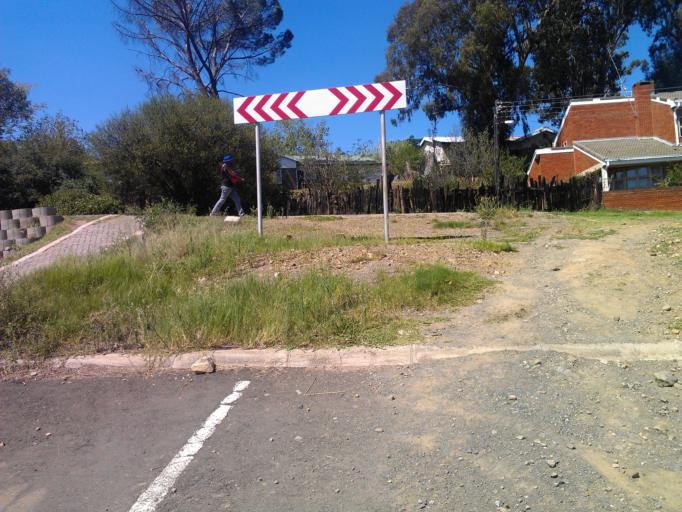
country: LS
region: Maseru
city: Maseru
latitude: -29.3102
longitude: 27.4781
